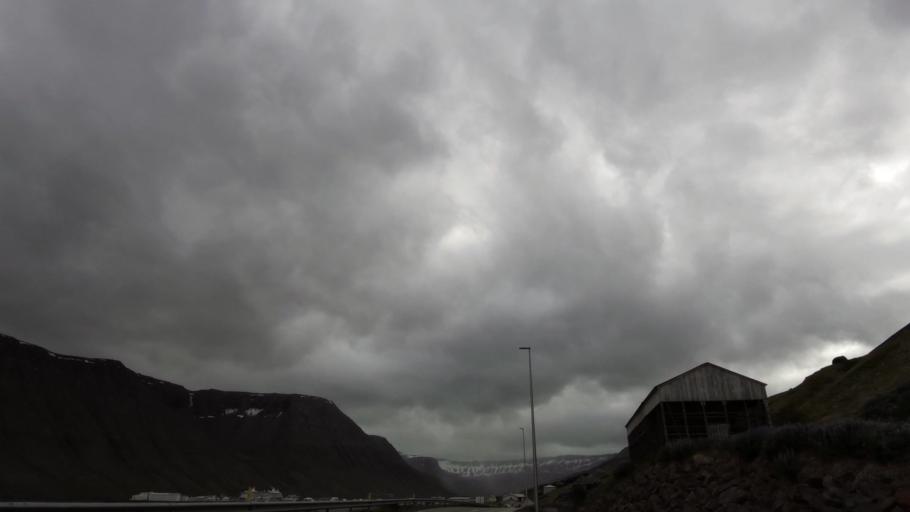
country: IS
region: Westfjords
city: Isafjoerdur
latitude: 66.0853
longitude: -23.1203
